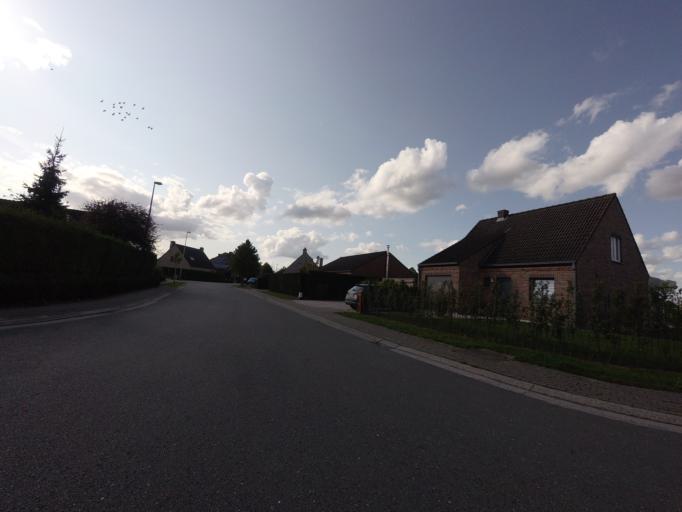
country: BE
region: Flanders
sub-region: Provincie Vlaams-Brabant
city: Londerzeel
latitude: 50.9876
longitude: 4.3268
